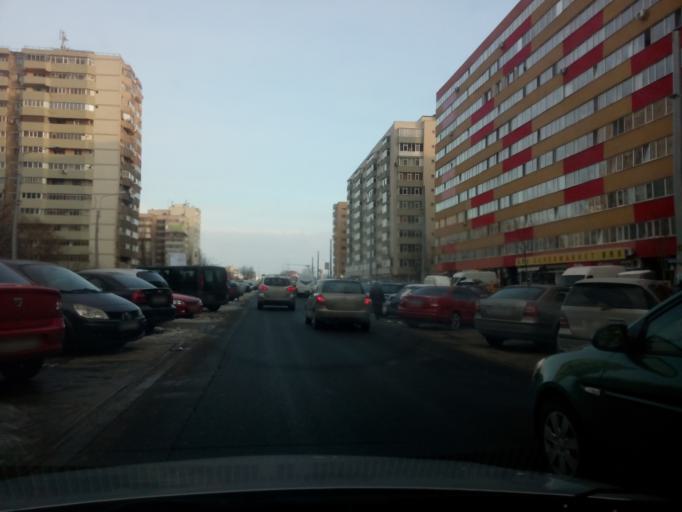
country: RO
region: Ilfov
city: Dobroesti
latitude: 44.4412
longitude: 26.1793
